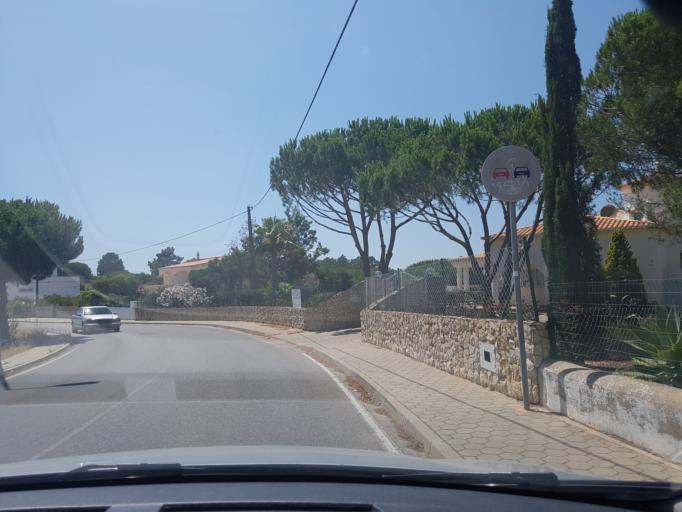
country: PT
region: Faro
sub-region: Lagoa
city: Carvoeiro
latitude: 37.1053
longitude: -8.4375
